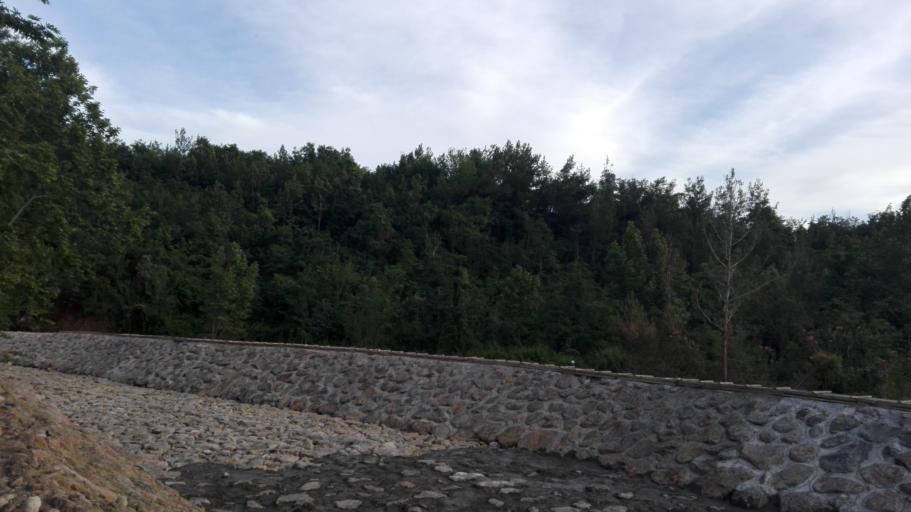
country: TR
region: Osmaniye
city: Haruniye
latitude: 37.2798
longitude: 36.4689
